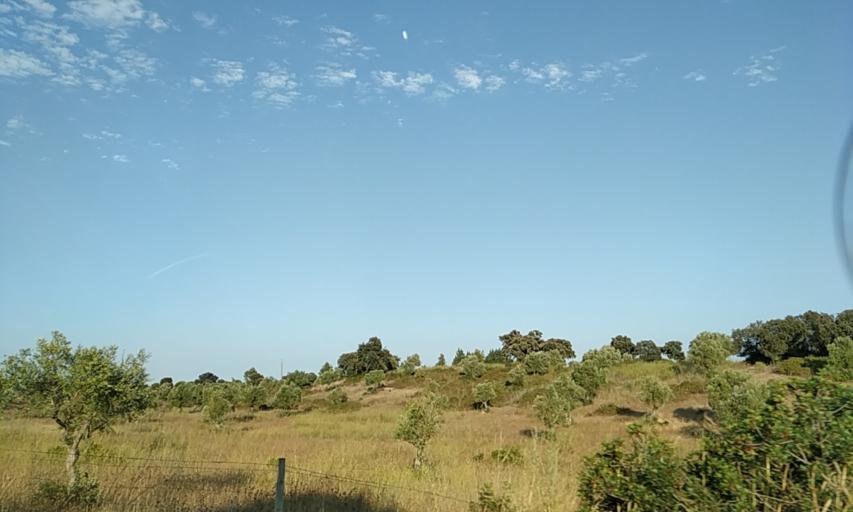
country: PT
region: Santarem
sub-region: Alcanena
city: Alcanena
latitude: 39.3954
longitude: -8.6452
